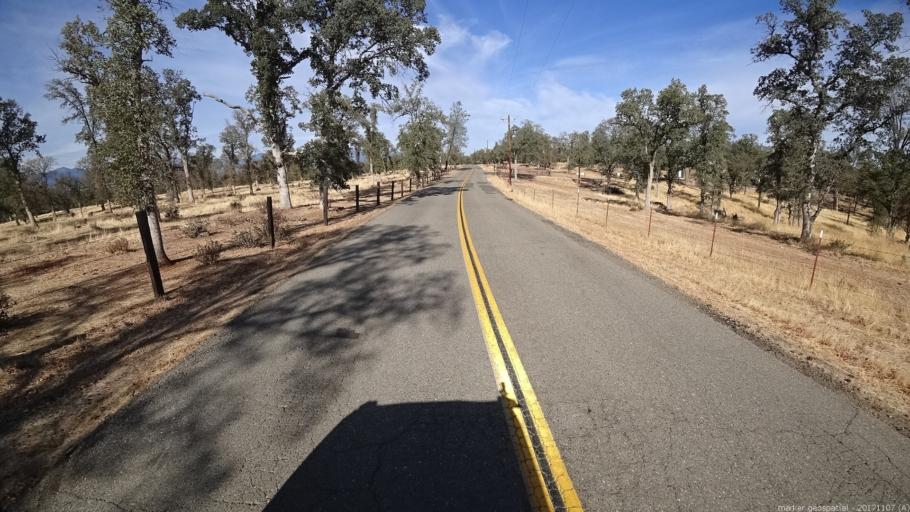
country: US
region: California
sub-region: Shasta County
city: Shasta
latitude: 40.4148
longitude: -122.5229
